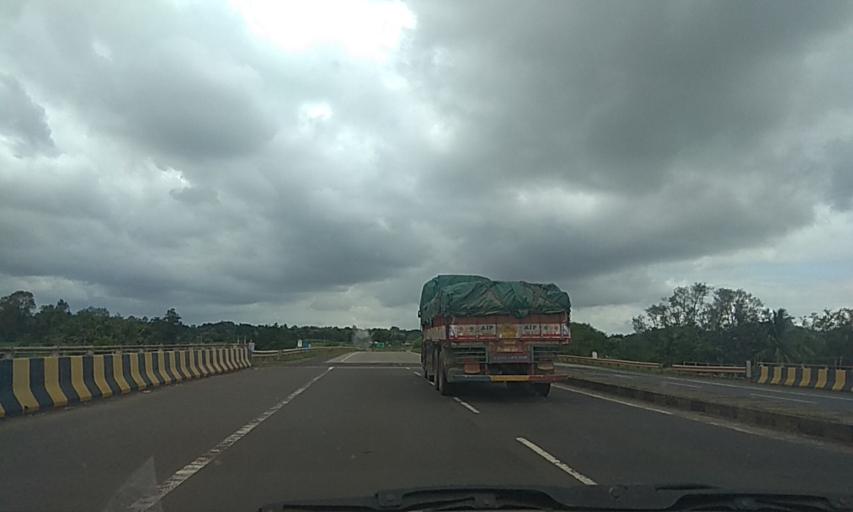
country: IN
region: Karnataka
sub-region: Belgaum
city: Sankeshwar
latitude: 16.2501
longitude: 74.4771
